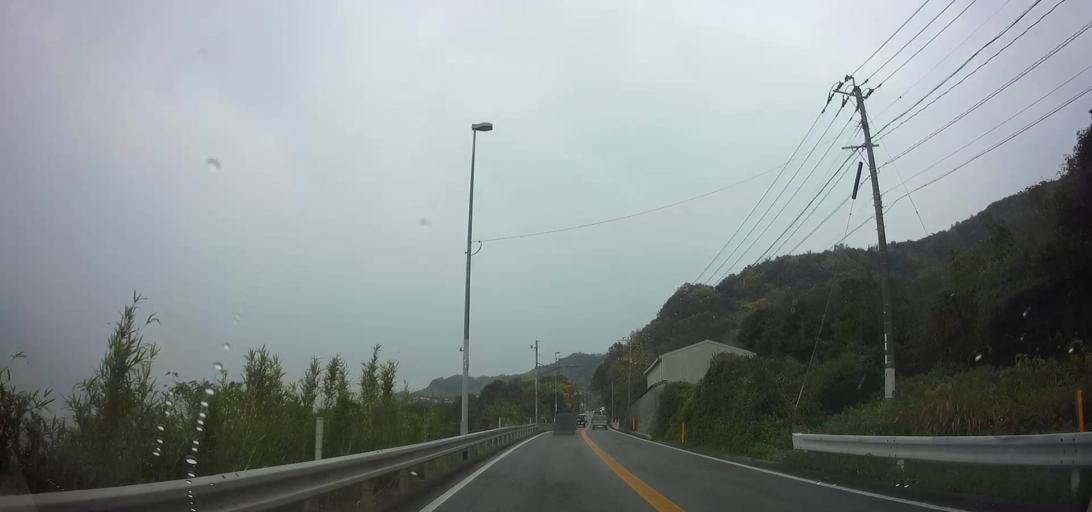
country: JP
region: Nagasaki
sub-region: Isahaya-shi
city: Isahaya
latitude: 32.7953
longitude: 130.1802
